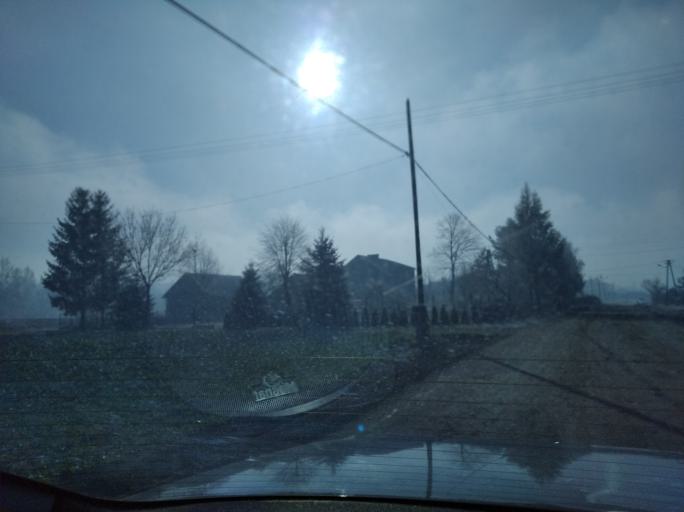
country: PL
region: Subcarpathian Voivodeship
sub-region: Powiat strzyzowski
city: Wisniowa
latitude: 49.8706
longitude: 21.7063
